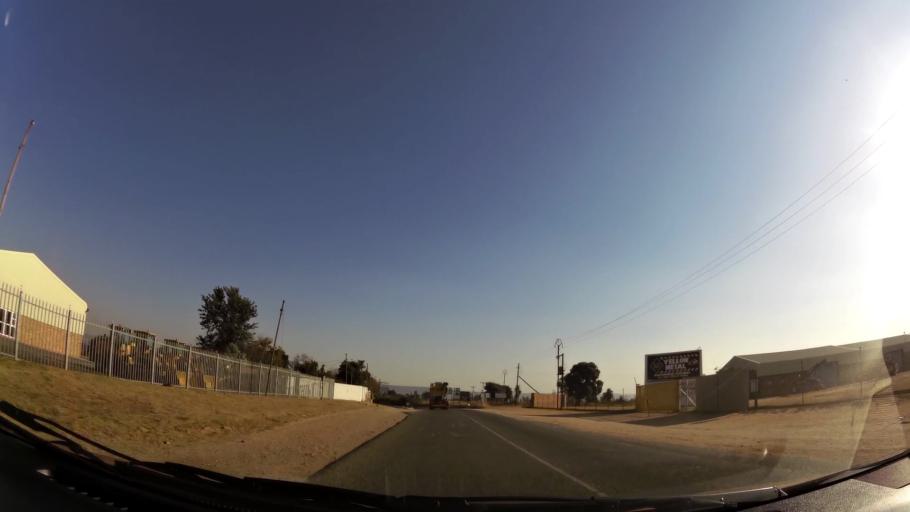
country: ZA
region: Gauteng
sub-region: West Rand District Municipality
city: Muldersdriseloop
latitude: -26.0254
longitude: 27.8696
